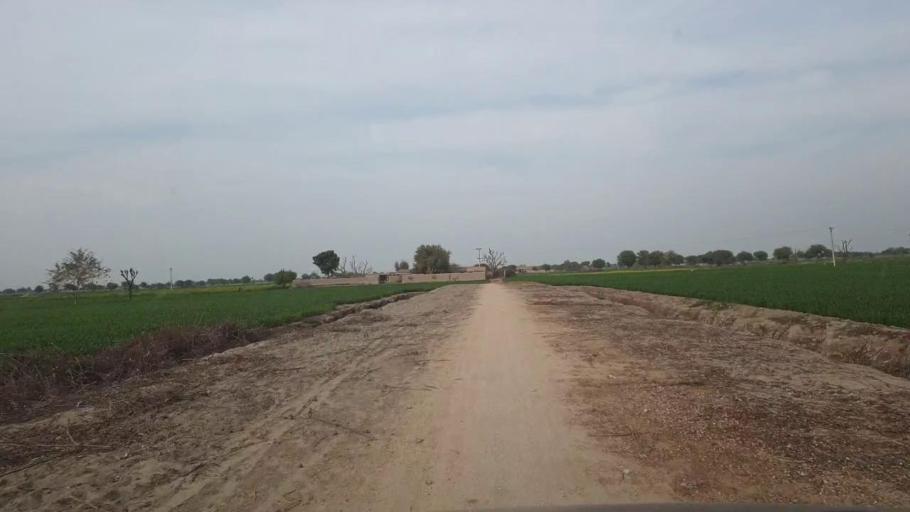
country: PK
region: Sindh
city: Shahpur Chakar
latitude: 26.1202
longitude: 68.5131
